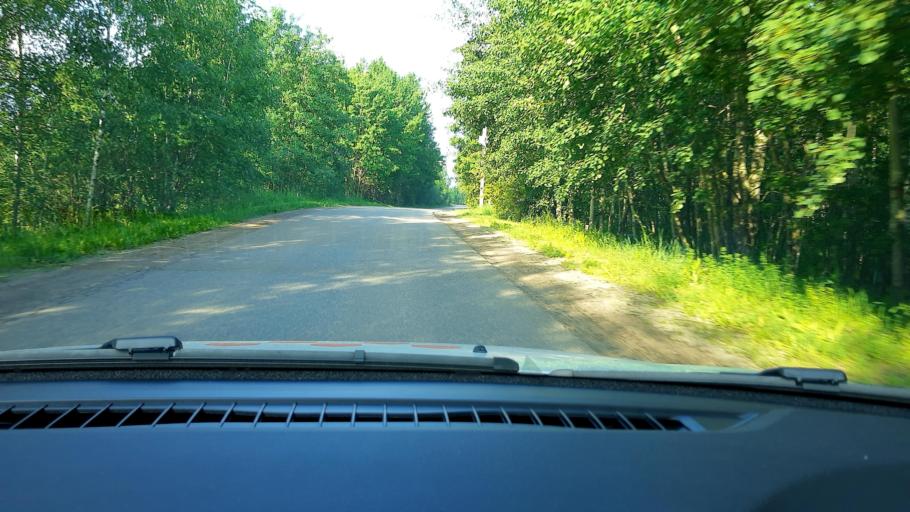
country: RU
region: Nizjnij Novgorod
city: Burevestnik
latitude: 56.1257
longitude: 43.9029
